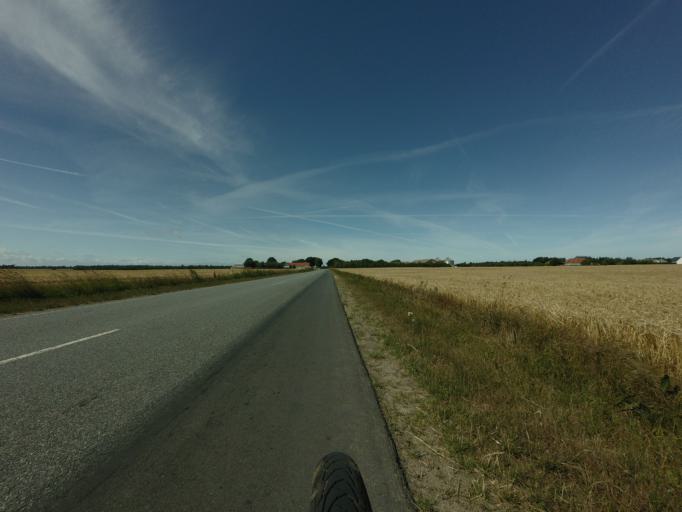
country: DK
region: North Denmark
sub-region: Hjorring Kommune
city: Vra
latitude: 57.3322
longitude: 9.8131
